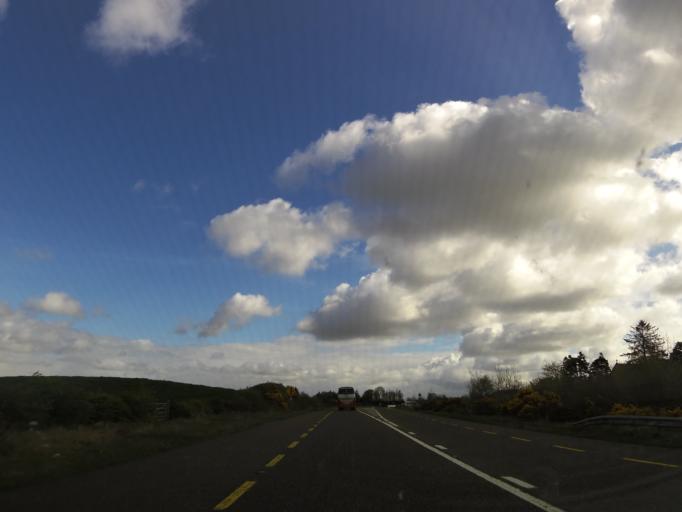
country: IE
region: Connaught
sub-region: Maigh Eo
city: Kiltamagh
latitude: 53.8196
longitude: -8.8921
